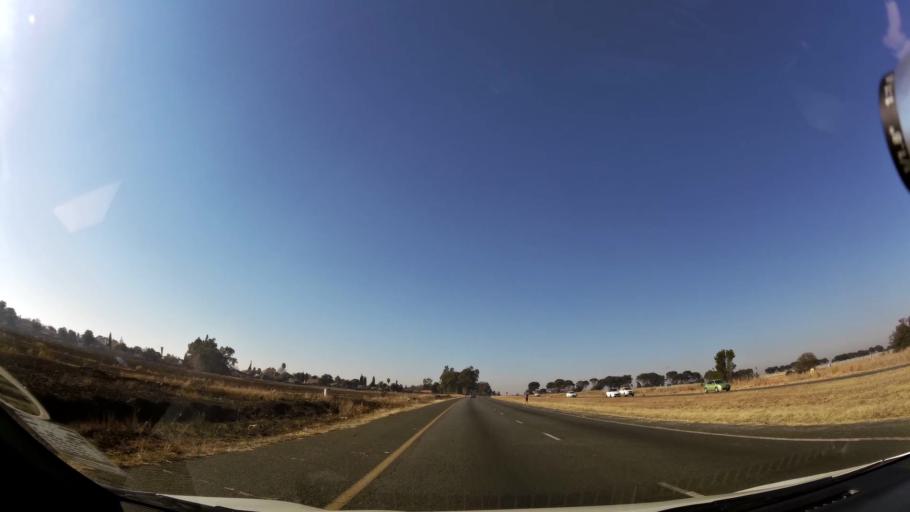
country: ZA
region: Gauteng
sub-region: City of Johannesburg Metropolitan Municipality
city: Johannesburg
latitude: -26.3328
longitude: 28.0778
